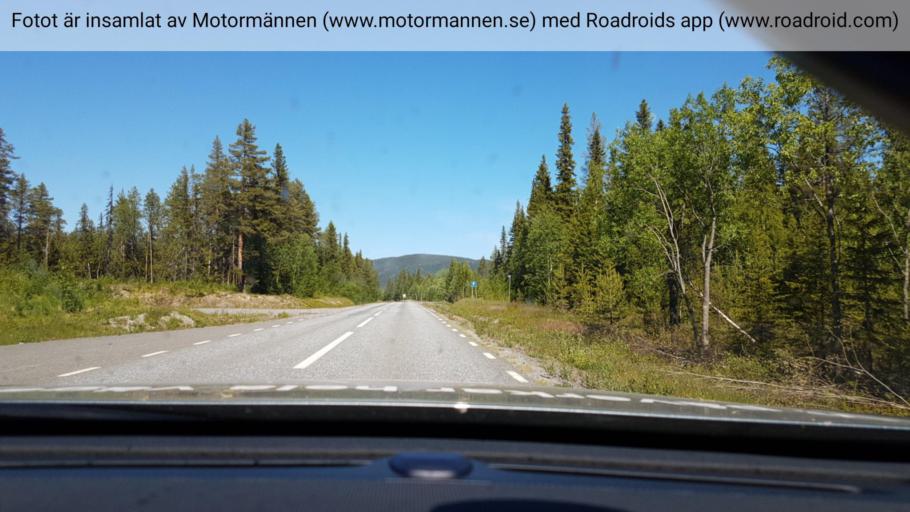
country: SE
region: Vaesterbotten
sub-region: Vilhelmina Kommun
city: Sjoberg
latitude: 64.9118
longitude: 15.8703
